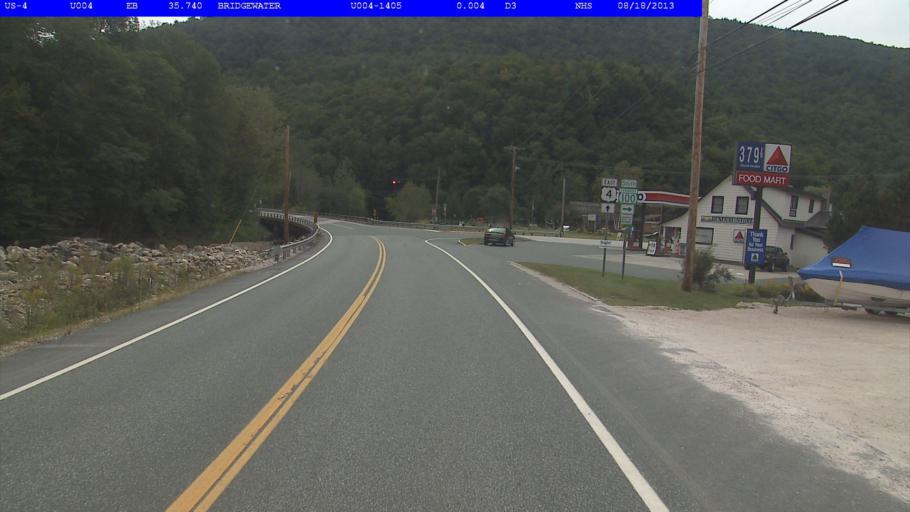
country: US
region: Vermont
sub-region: Rutland County
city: Rutland
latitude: 43.6004
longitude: -72.7496
